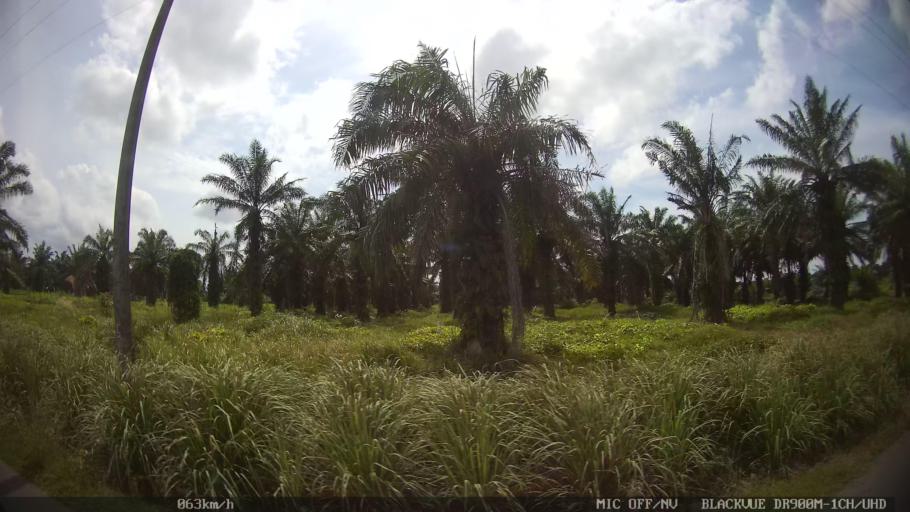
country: ID
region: North Sumatra
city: Percut
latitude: 3.5871
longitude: 98.8410
